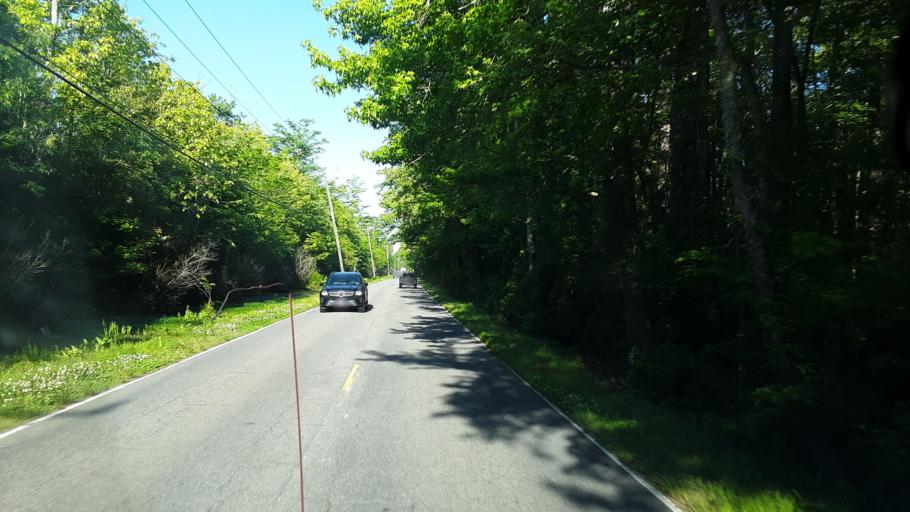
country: US
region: Virginia
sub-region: City of Virginia Beach
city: Virginia Beach
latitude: 36.7224
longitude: -76.0270
